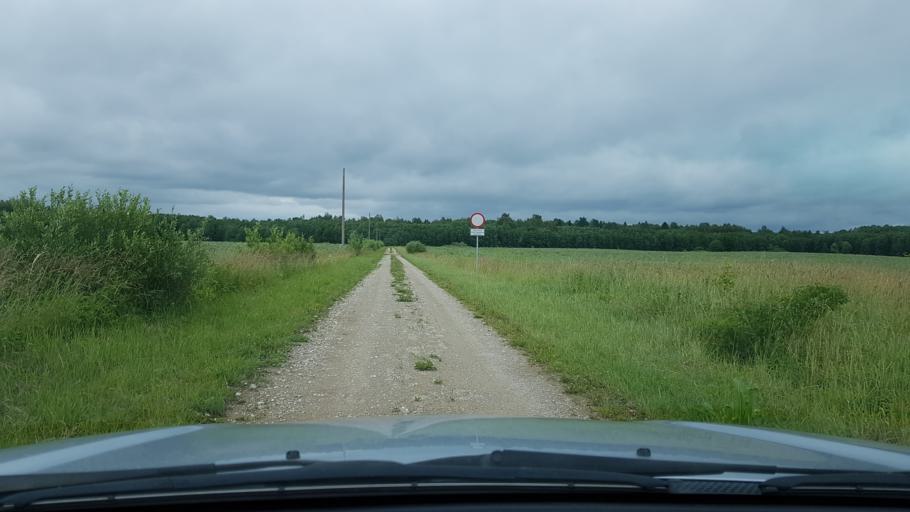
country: EE
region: Ida-Virumaa
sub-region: Narva-Joesuu linn
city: Narva-Joesuu
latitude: 59.3450
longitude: 27.9491
